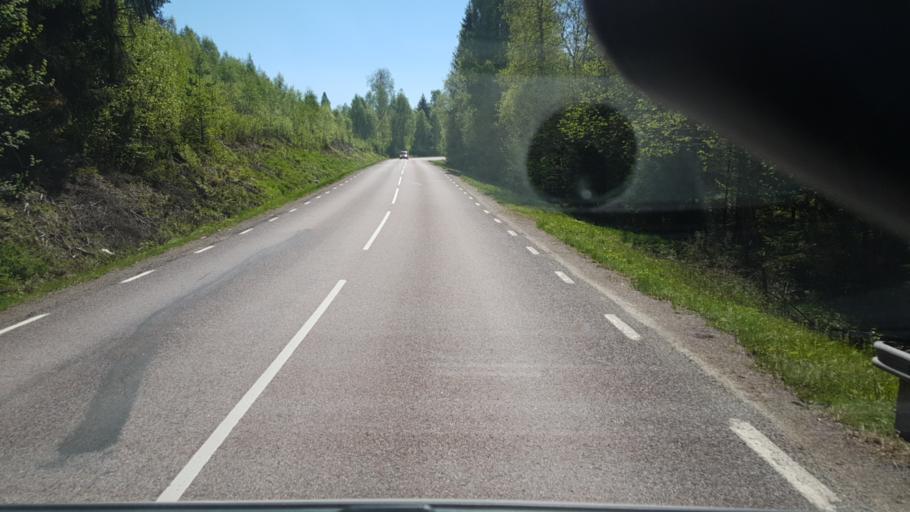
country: SE
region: Vaermland
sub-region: Eda Kommun
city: Amotfors
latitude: 59.8601
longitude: 12.5467
